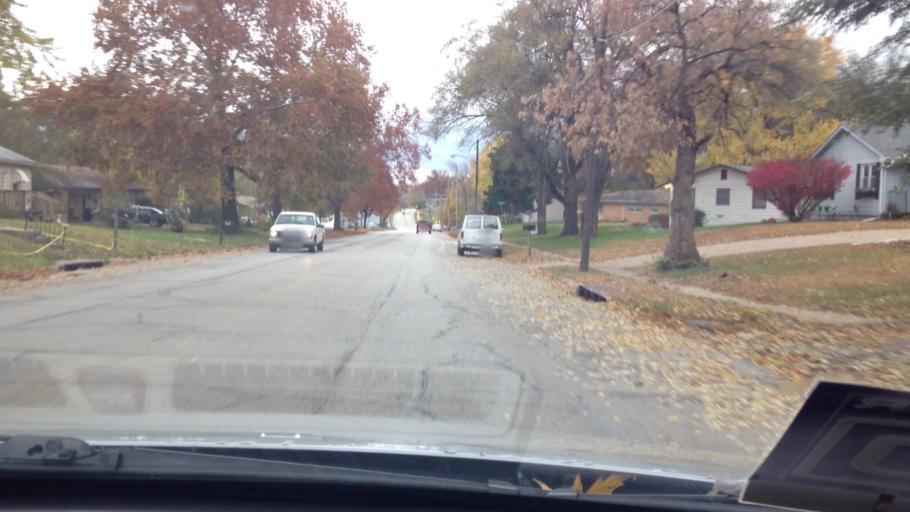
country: US
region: Kansas
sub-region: Leavenworth County
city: Leavenworth
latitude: 39.2992
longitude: -94.9137
